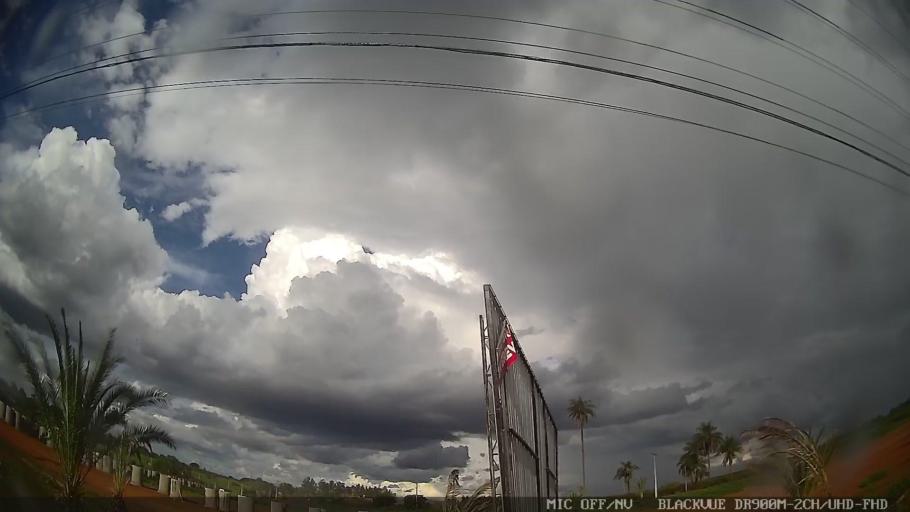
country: BR
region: Sao Paulo
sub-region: Jaguariuna
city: Jaguariuna
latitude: -22.6761
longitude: -47.0254
